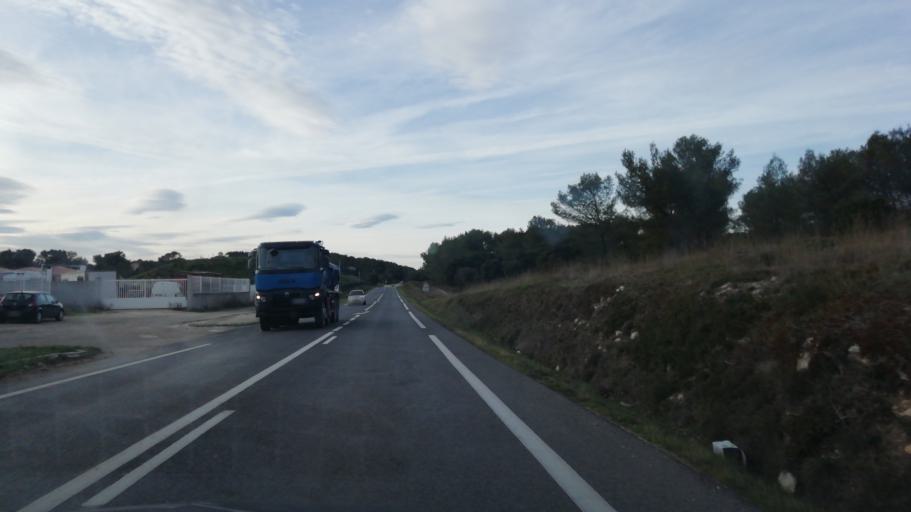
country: FR
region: Languedoc-Roussillon
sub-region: Departement du Gard
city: Caveirac
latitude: 43.8447
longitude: 4.3012
